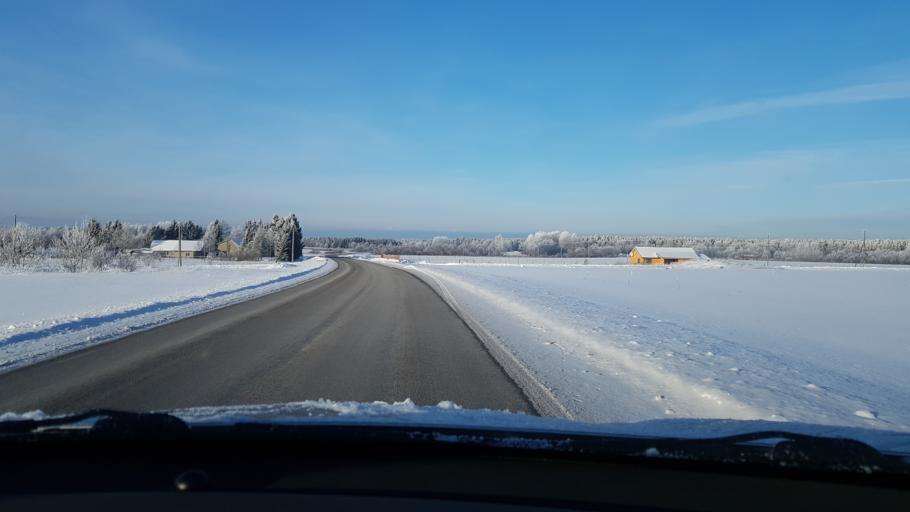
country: EE
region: Harju
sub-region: Harku vald
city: Tabasalu
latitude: 59.3668
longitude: 24.4825
